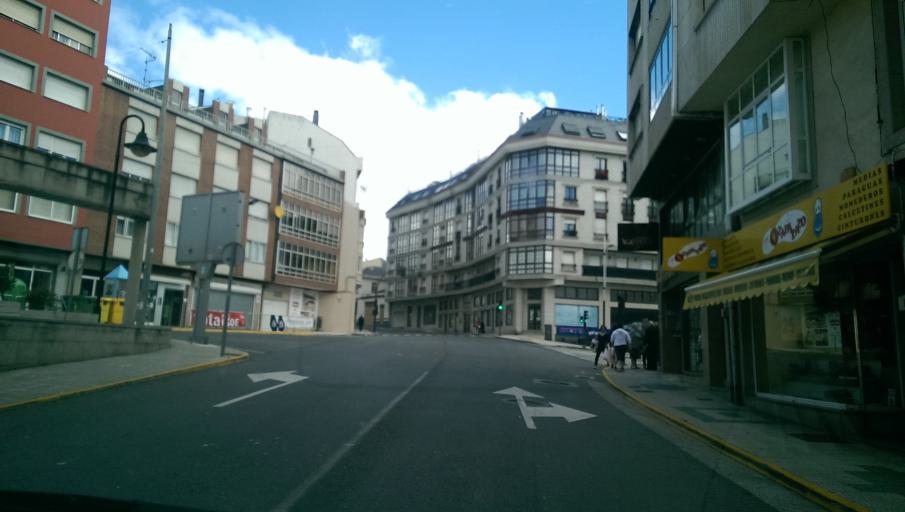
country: ES
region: Galicia
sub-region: Provincia de Lugo
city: Foz
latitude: 43.5690
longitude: -7.2582
